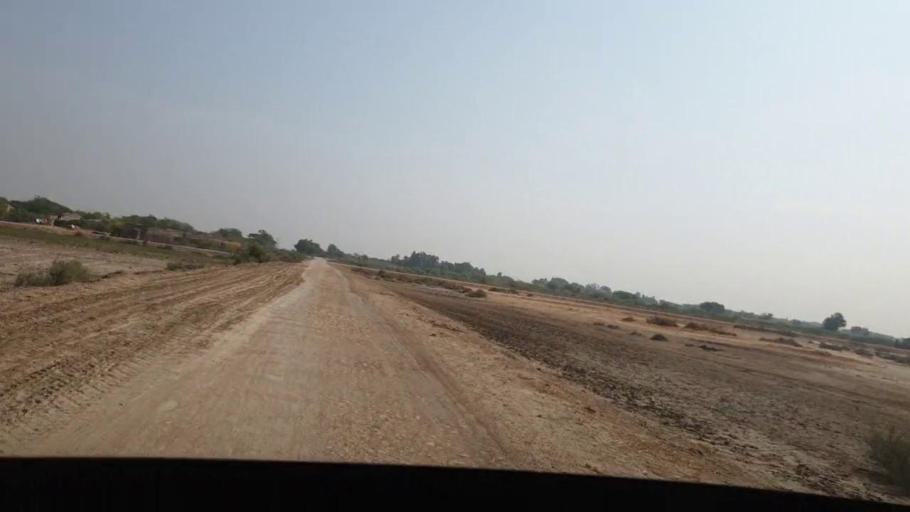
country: PK
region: Sindh
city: Chuhar Jamali
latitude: 24.2694
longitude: 67.9383
